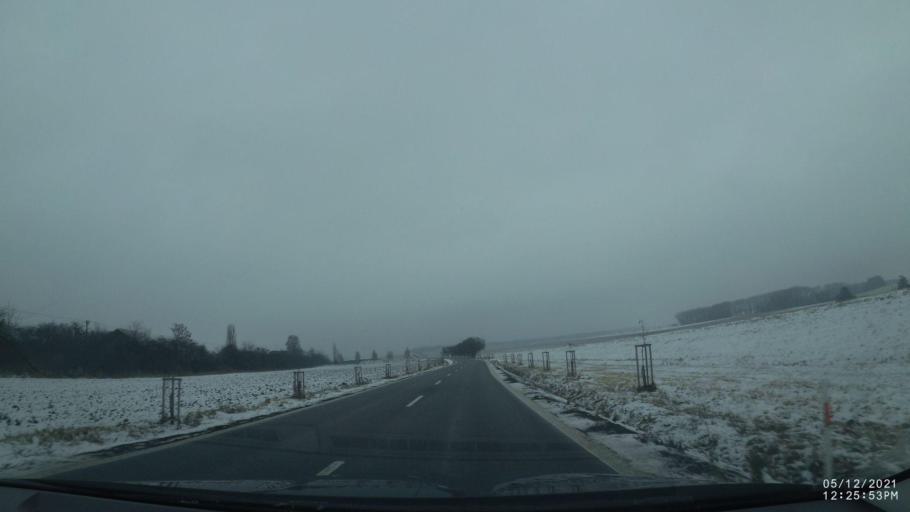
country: CZ
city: Nove Mesto nad Metuji
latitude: 50.3259
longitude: 16.0930
